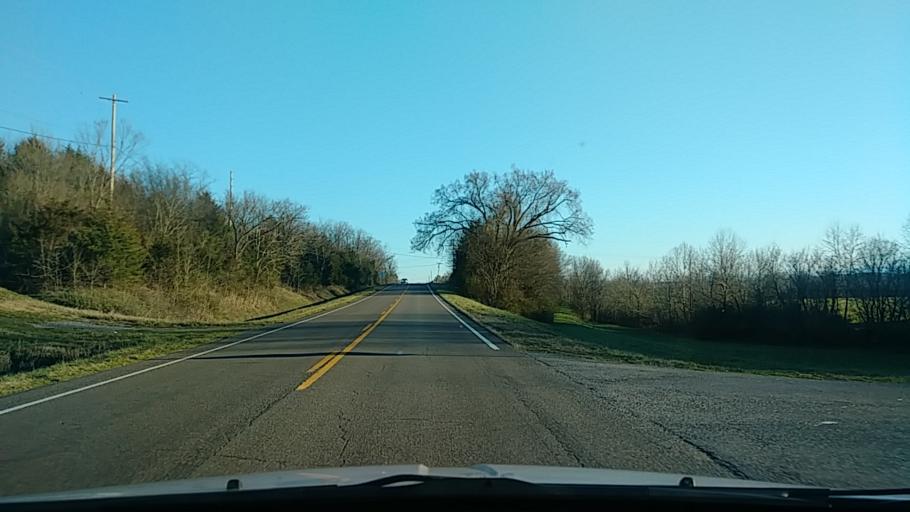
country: US
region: Tennessee
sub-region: Hamblen County
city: Morristown
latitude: 36.1894
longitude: -83.1707
